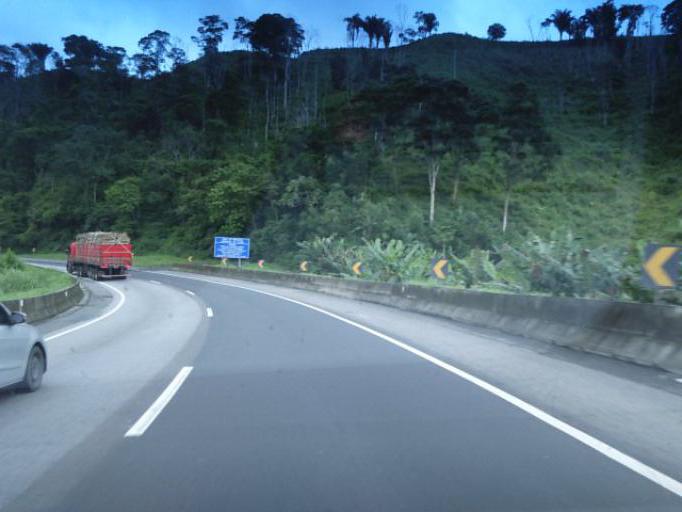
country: BR
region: Sao Paulo
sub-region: Cajati
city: Cajati
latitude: -24.8499
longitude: -48.2098
